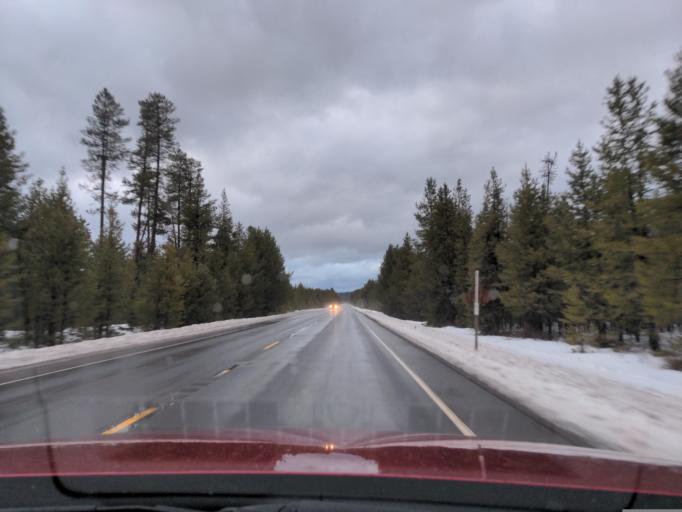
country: US
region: Oregon
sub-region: Deschutes County
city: La Pine
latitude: 43.4055
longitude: -121.8260
